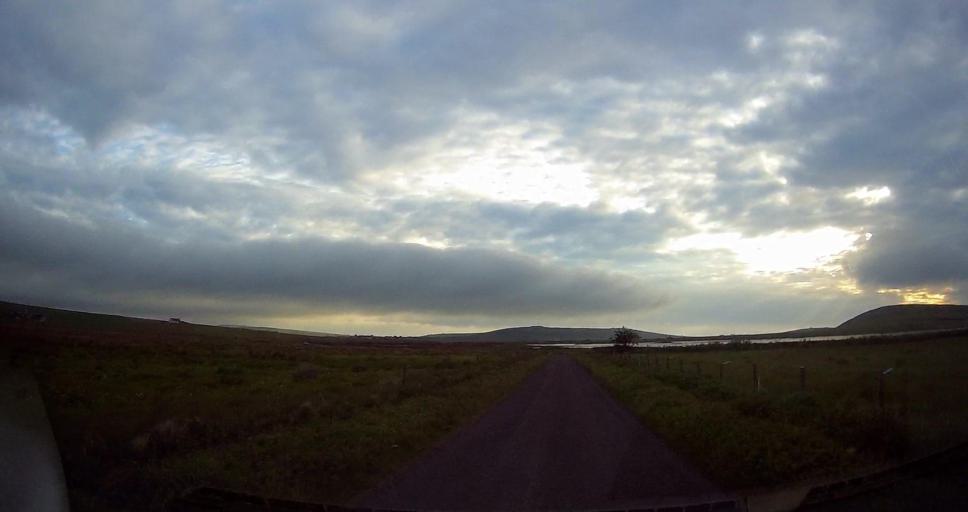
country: GB
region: Scotland
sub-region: Orkney Islands
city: Stromness
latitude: 59.1095
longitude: -3.2274
